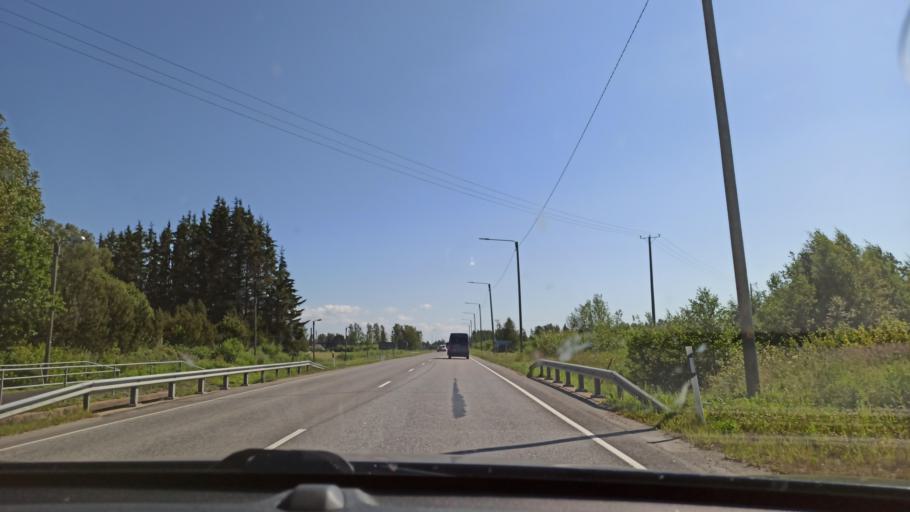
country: FI
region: Satakunta
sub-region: Pori
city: Pori
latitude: 61.5214
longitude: 21.8031
